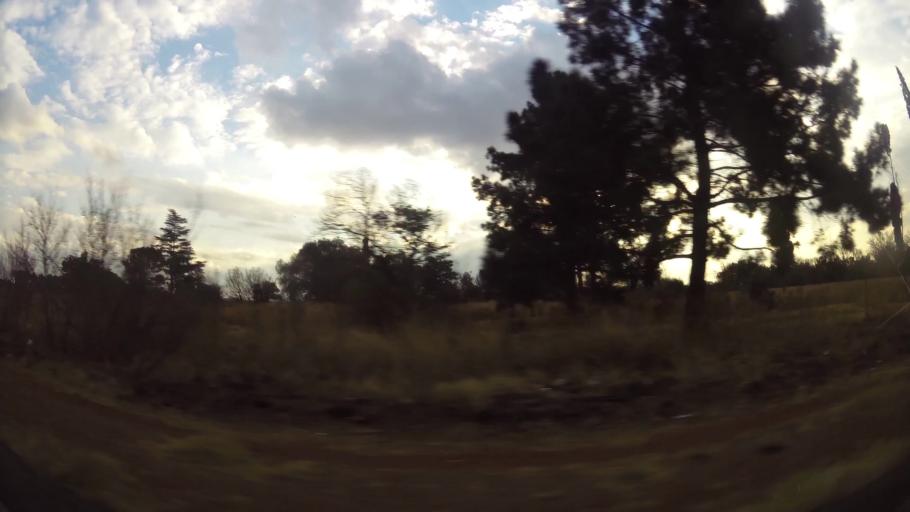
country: ZA
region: Gauteng
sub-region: Sedibeng District Municipality
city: Vanderbijlpark
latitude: -26.6370
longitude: 27.8069
